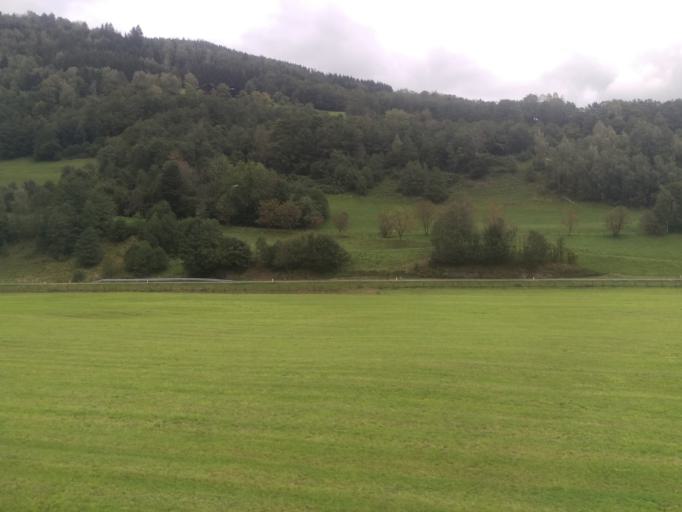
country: AT
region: Salzburg
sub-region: Politischer Bezirk Zell am See
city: Niedernsill
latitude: 47.2846
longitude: 12.6768
